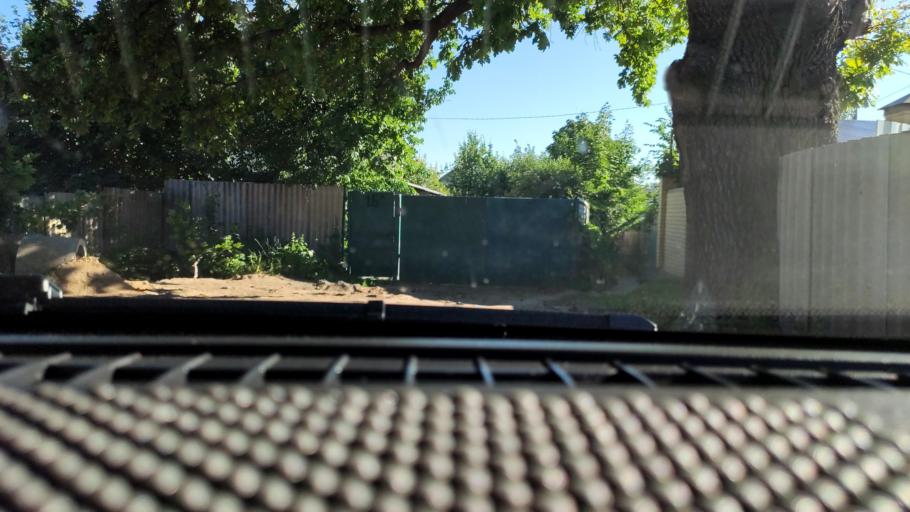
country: RU
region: Voronezj
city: Podgornoye
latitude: 51.7389
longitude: 39.1515
